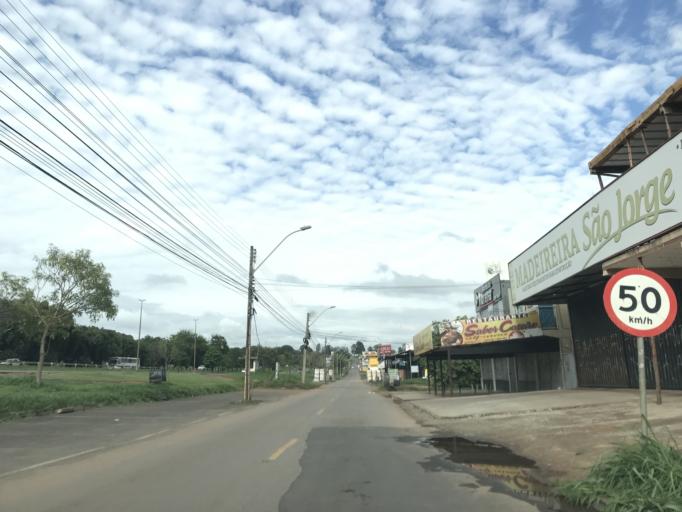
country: BR
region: Federal District
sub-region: Brasilia
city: Brasilia
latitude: -15.6601
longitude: -47.7946
